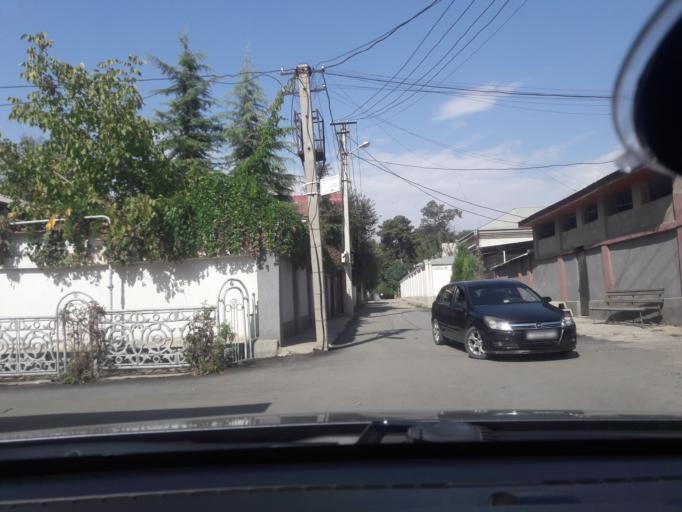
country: TJ
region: Dushanbe
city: Dushanbe
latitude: 38.5763
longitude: 68.7969
